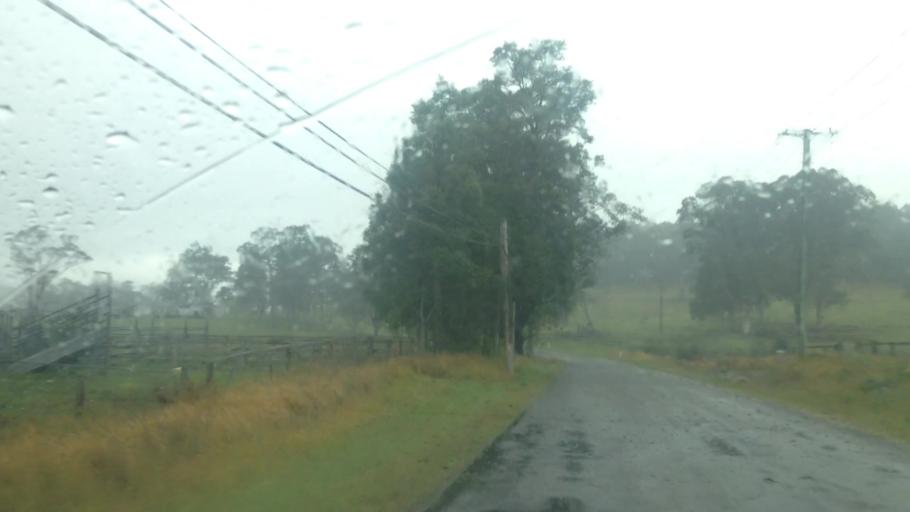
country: AU
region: New South Wales
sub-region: Wyong Shire
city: Little Jilliby
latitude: -33.1948
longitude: 151.3576
